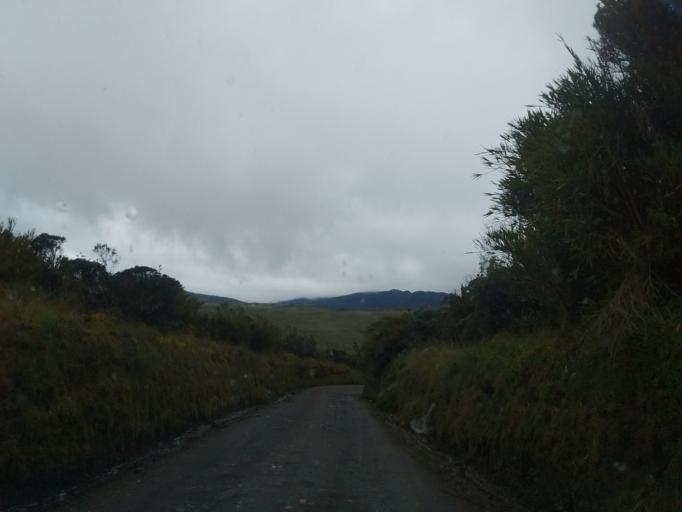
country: CO
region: Cauca
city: Totoro
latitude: 2.3568
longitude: -76.3326
